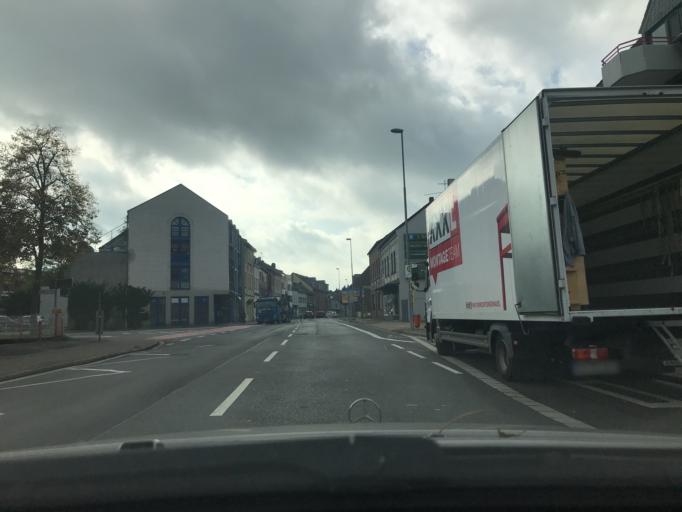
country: DE
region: North Rhine-Westphalia
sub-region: Regierungsbezirk Dusseldorf
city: Moers
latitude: 51.4570
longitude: 6.6295
